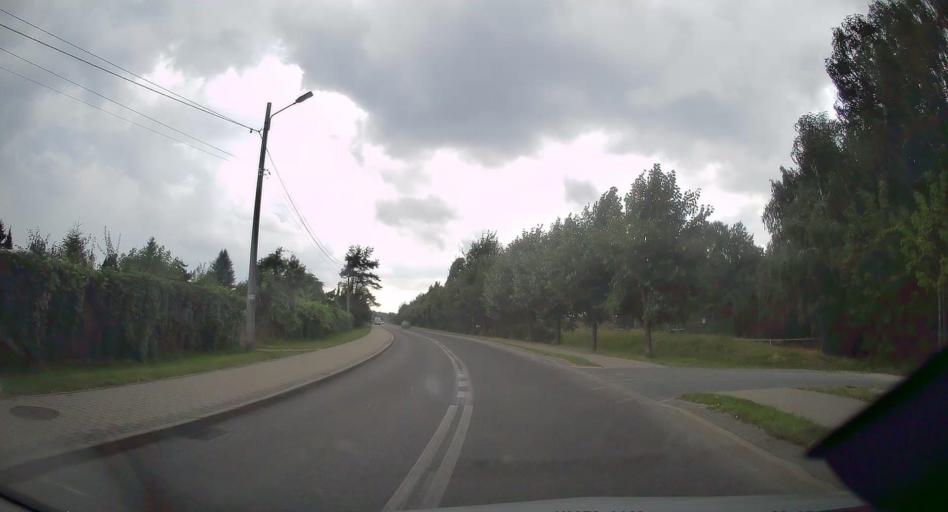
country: PL
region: Lodz Voivodeship
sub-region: Powiat rawski
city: Rawa Mazowiecka
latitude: 51.7533
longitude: 20.2315
